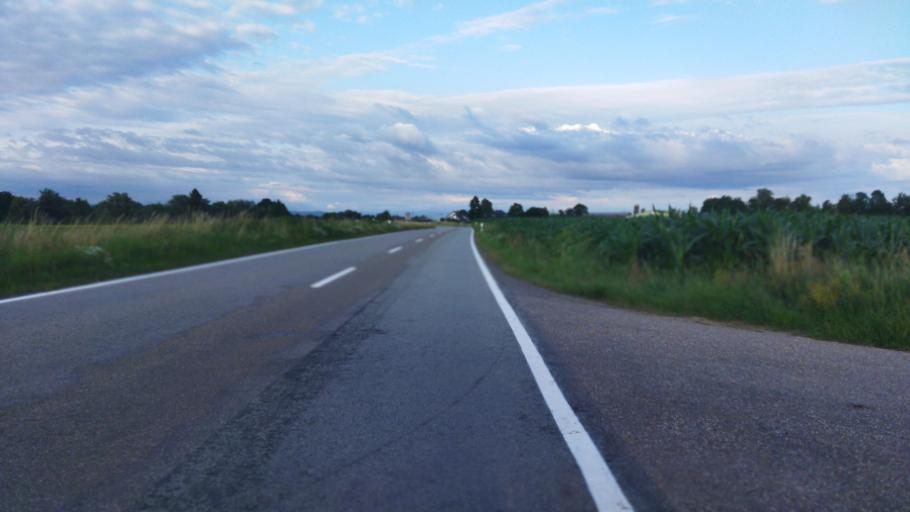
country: DE
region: Bavaria
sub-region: Upper Palatinate
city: Riekofen
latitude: 48.9647
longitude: 12.3205
